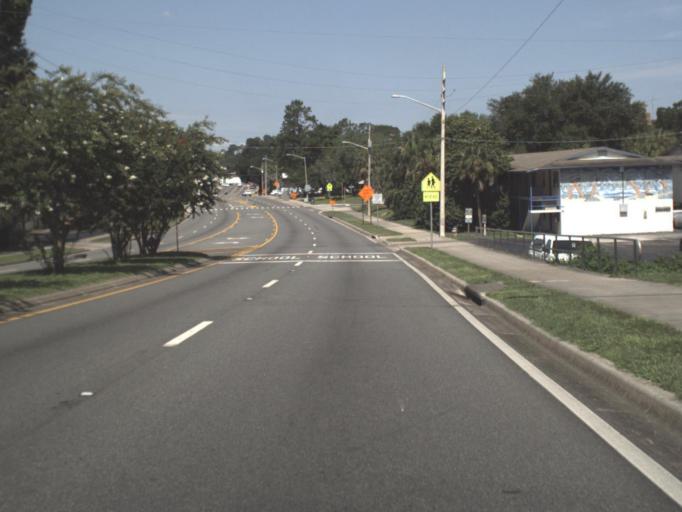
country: US
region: Florida
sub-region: Alachua County
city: Gainesville
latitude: 29.6367
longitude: -82.3337
